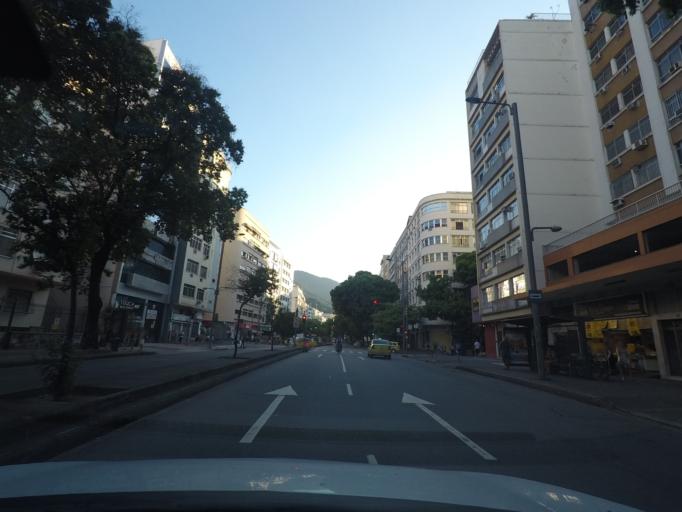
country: BR
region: Rio de Janeiro
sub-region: Rio De Janeiro
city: Rio de Janeiro
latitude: -22.9275
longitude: -43.2360
